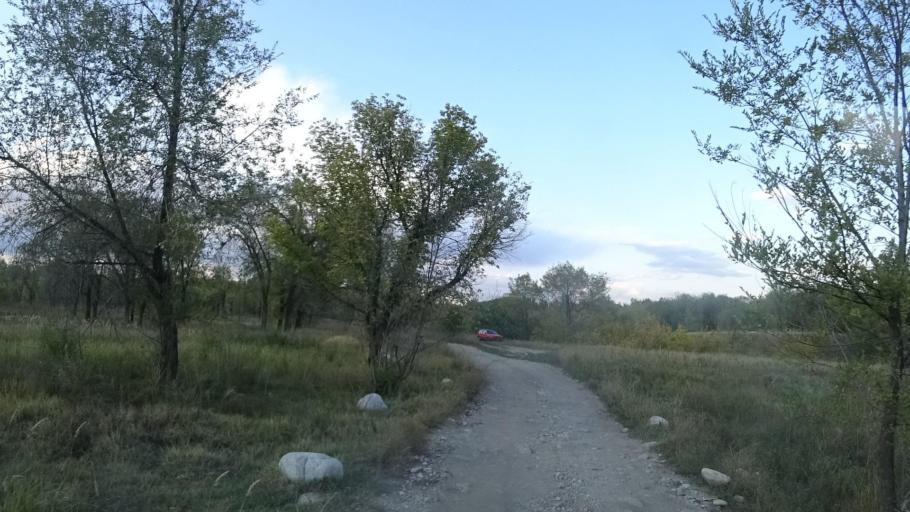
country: KZ
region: Almaty Oblysy
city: Pervomayskiy
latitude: 43.3334
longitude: 76.9993
